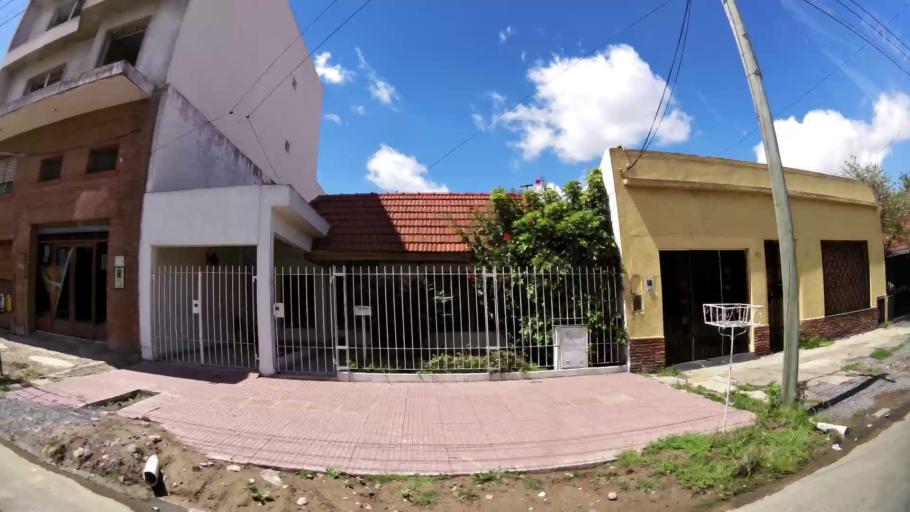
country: AR
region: Buenos Aires
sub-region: Partido de Lanus
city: Lanus
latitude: -34.7013
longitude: -58.4208
